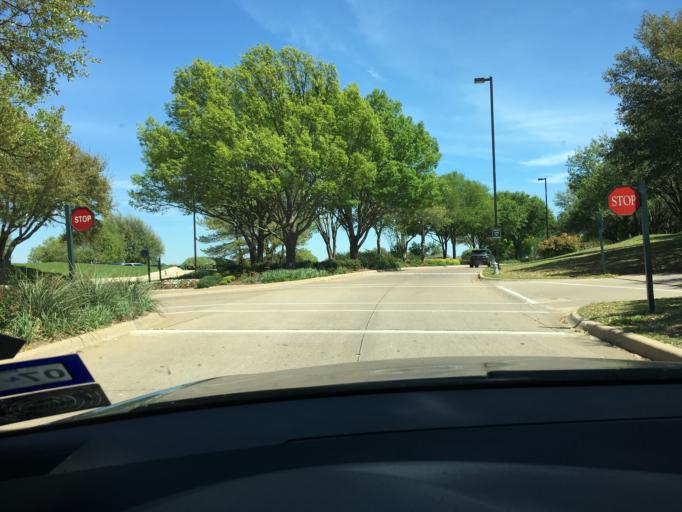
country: US
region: Texas
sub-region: Tarrant County
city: Benbrook
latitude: 32.6578
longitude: -97.4351
